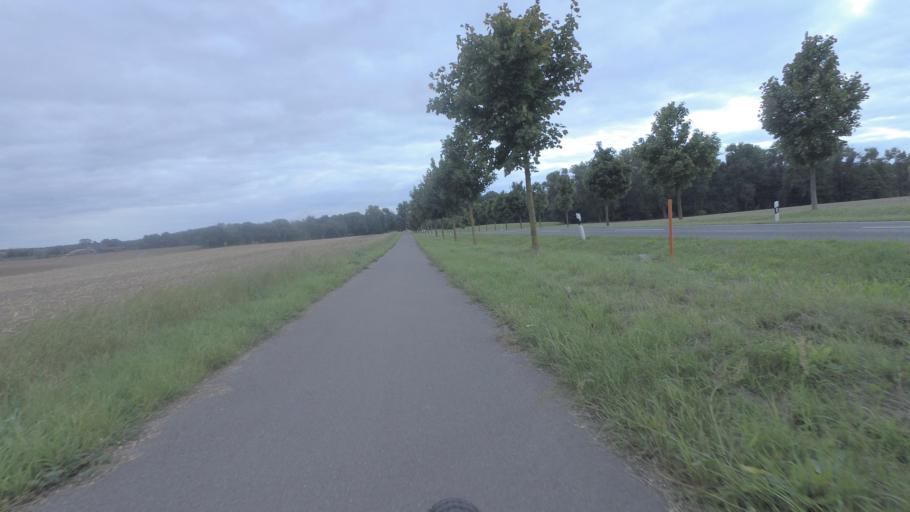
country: DE
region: Brandenburg
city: Altlandsberg
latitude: 52.6025
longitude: 13.6864
